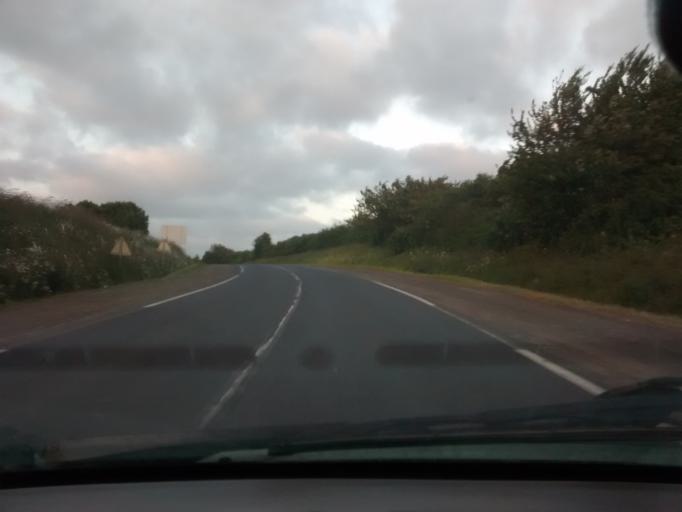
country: FR
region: Lower Normandy
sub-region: Departement de la Manche
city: Saint-Lo
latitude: 49.0990
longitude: -1.0921
